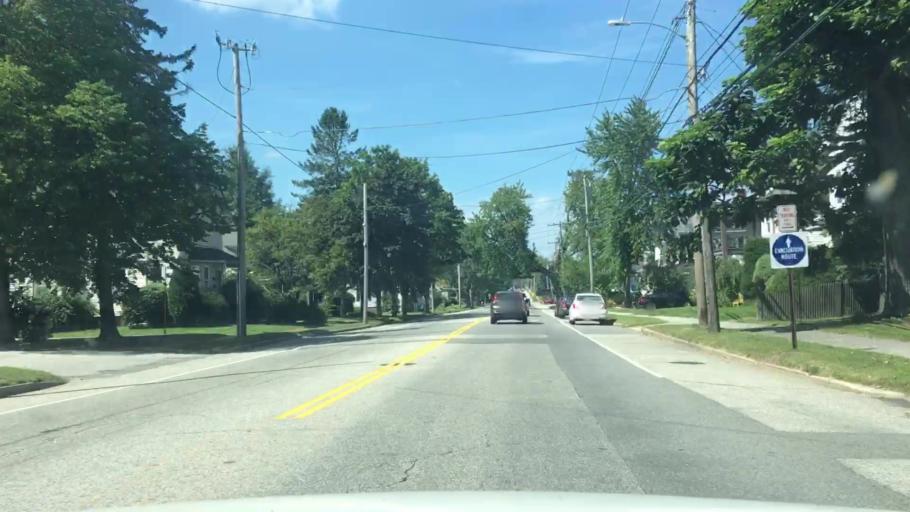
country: US
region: Maine
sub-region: Cumberland County
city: Portland
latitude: 43.6869
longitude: -70.2701
